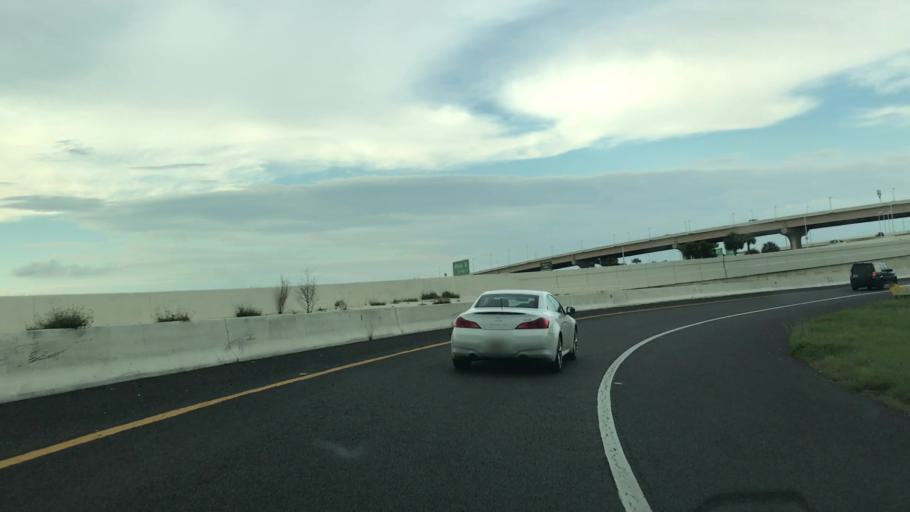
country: US
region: Florida
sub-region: Hillsborough County
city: Town 'n' Country
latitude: 27.9565
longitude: -82.5415
